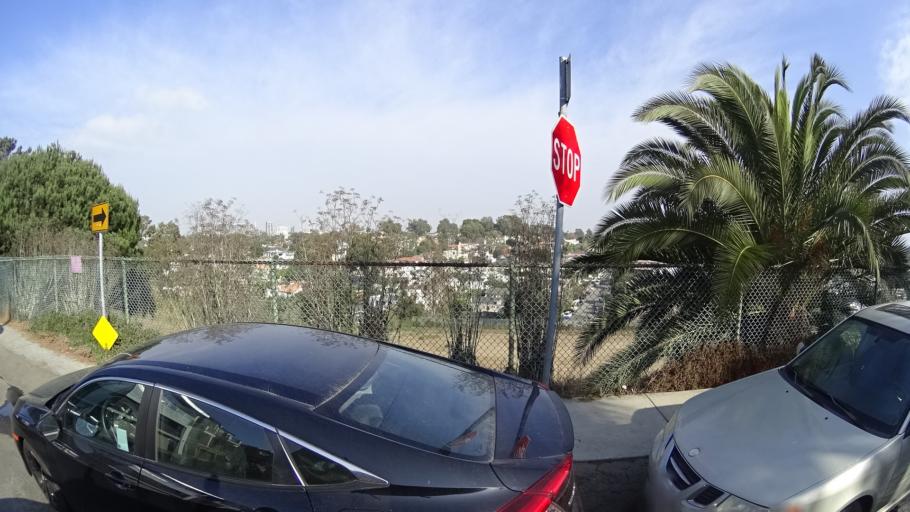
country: US
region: California
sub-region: Los Angeles County
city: Manhattan Beach
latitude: 33.8968
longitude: -118.4127
